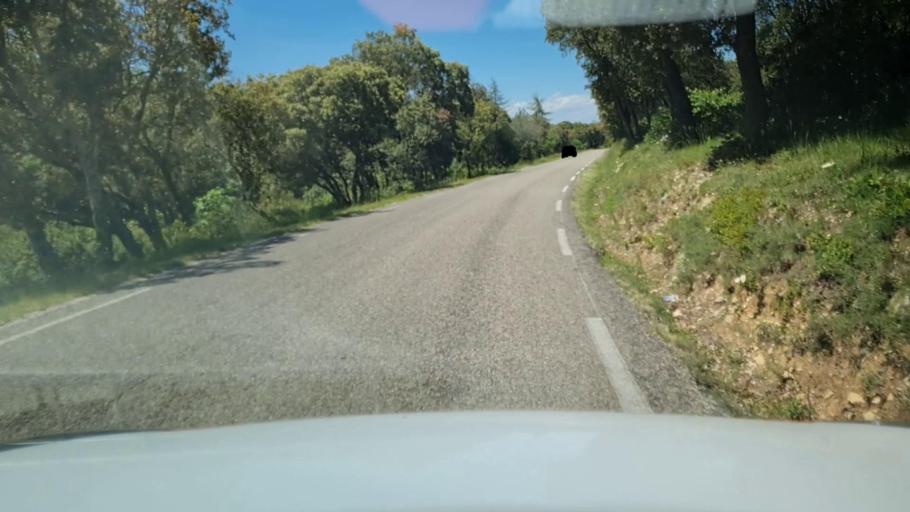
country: FR
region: Languedoc-Roussillon
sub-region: Departement du Gard
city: Clarensac
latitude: 43.8550
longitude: 4.2154
